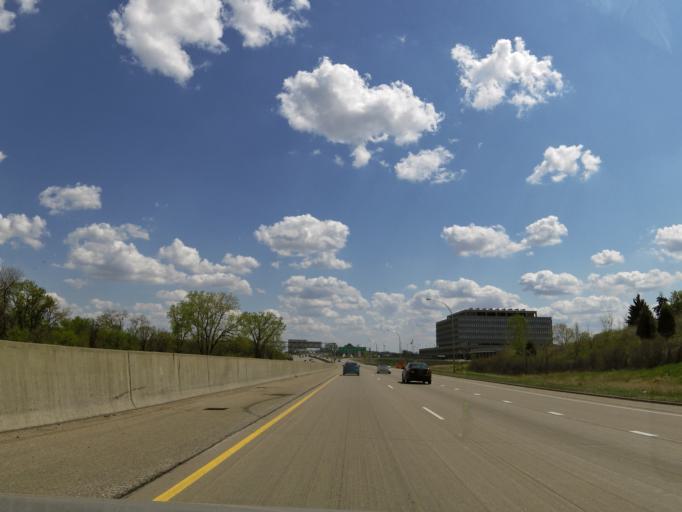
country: US
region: Minnesota
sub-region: Dakota County
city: Mendota Heights
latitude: 44.8974
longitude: -93.1976
